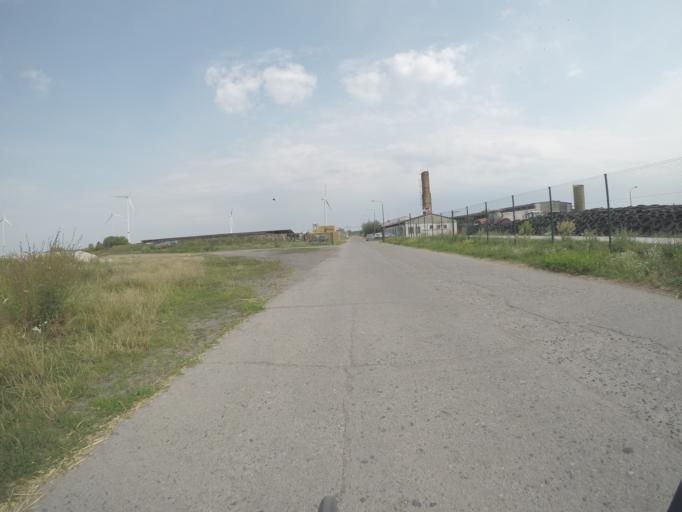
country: DE
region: Berlin
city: Blankenfelde
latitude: 52.6597
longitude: 13.4251
